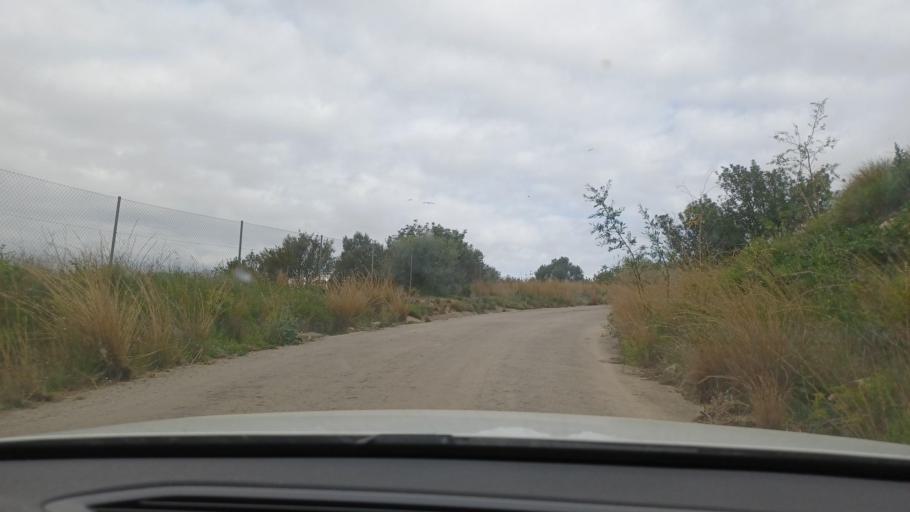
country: ES
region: Catalonia
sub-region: Provincia de Tarragona
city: Tortosa
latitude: 40.7898
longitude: 0.4888
